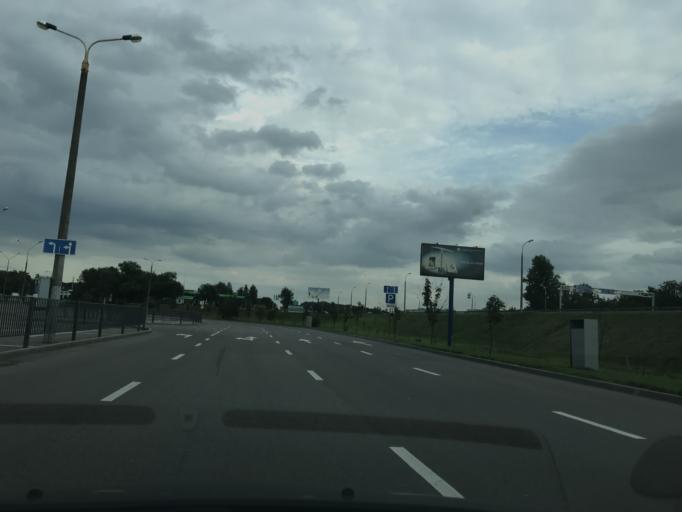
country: BY
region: Minsk
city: Borovlyany
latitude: 53.9623
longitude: 27.6218
